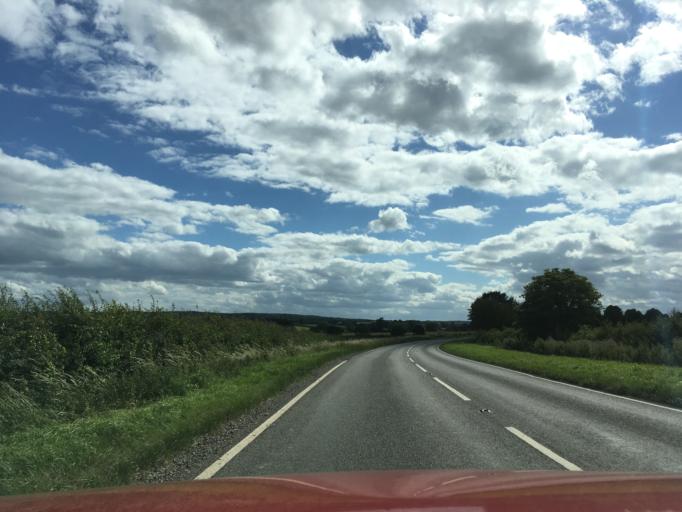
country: GB
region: England
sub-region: Leicestershire
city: Shepshed
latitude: 52.7909
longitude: -1.3074
